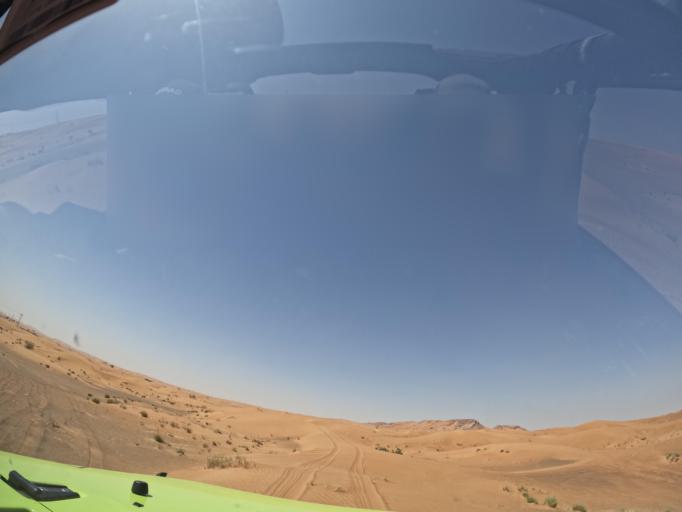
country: AE
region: Ash Shariqah
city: Adh Dhayd
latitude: 25.0190
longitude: 55.7469
